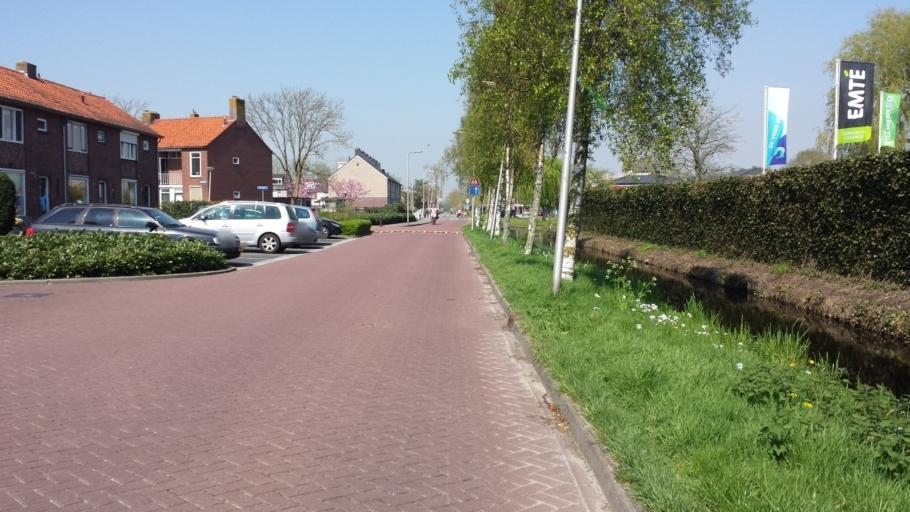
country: NL
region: South Holland
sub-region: Gemeente Vlist
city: Haastrecht
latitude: 51.9754
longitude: 4.7713
